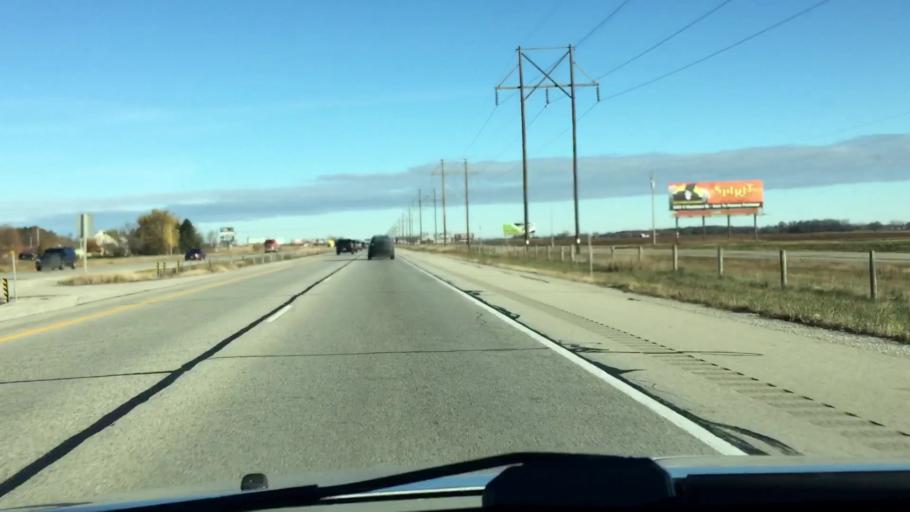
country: US
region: Wisconsin
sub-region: Winnebago County
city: Oshkosh
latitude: 43.9123
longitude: -88.5833
